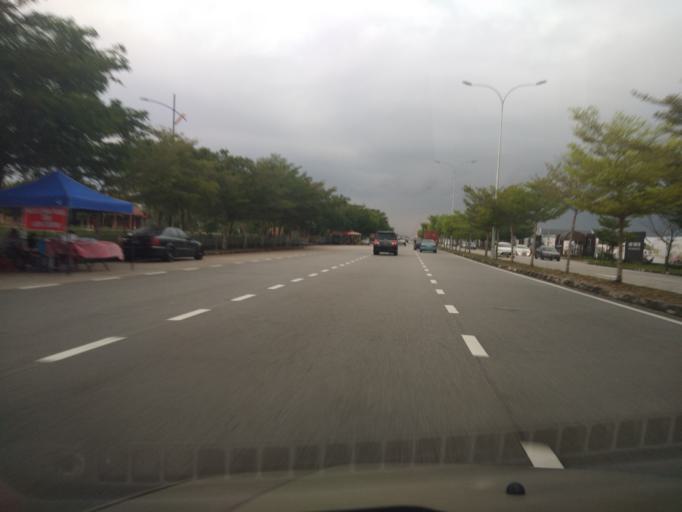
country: MY
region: Penang
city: Kepala Batas
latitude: 5.5182
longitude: 100.4522
